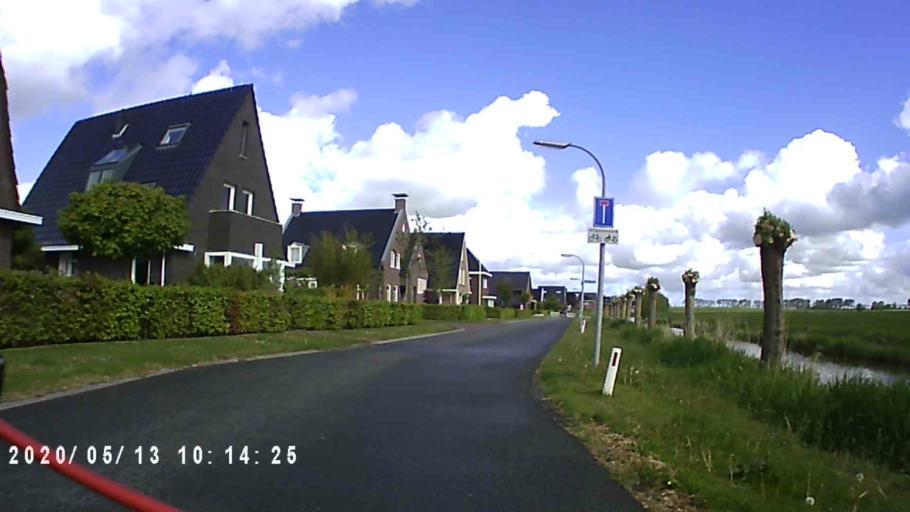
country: NL
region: Groningen
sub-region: Gemeente Zuidhorn
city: Zuidhorn
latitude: 53.2467
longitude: 6.4170
